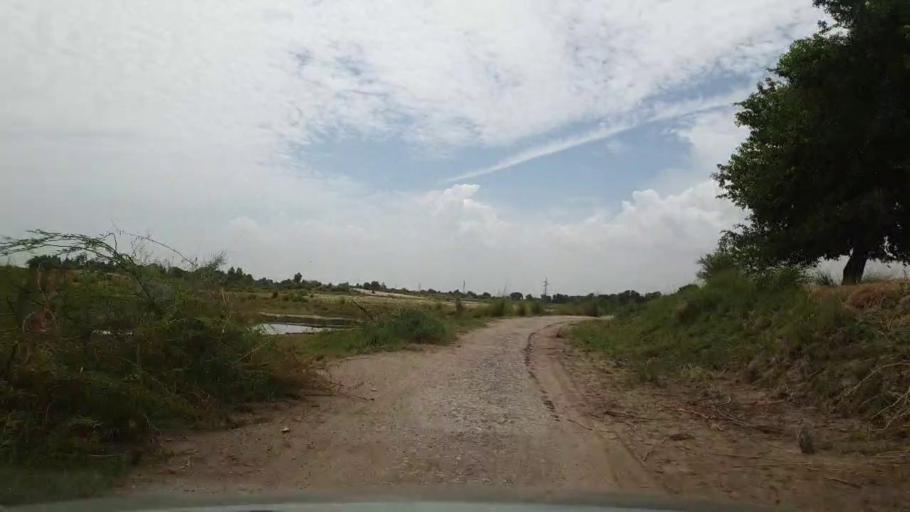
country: PK
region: Sindh
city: Bozdar
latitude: 27.0581
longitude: 68.9725
